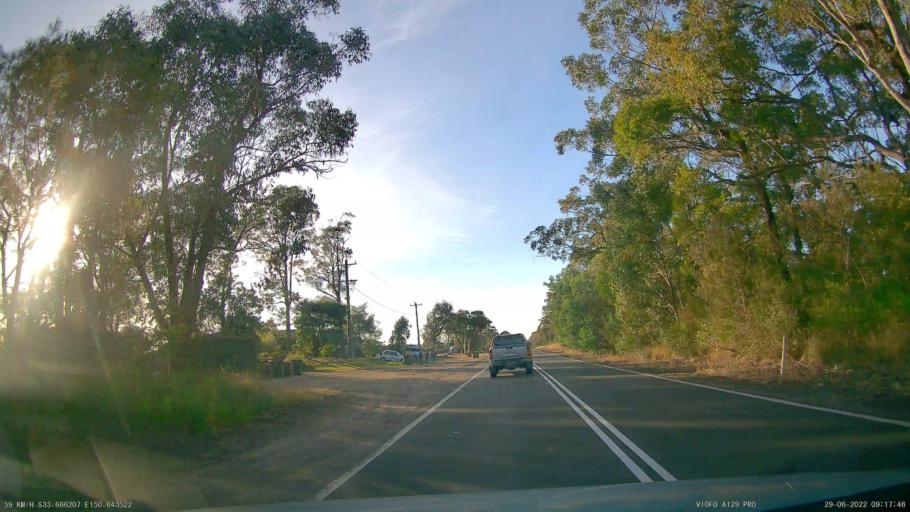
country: AU
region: New South Wales
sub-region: Penrith Municipality
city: Emu Heights
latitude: -33.6663
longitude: 150.6439
